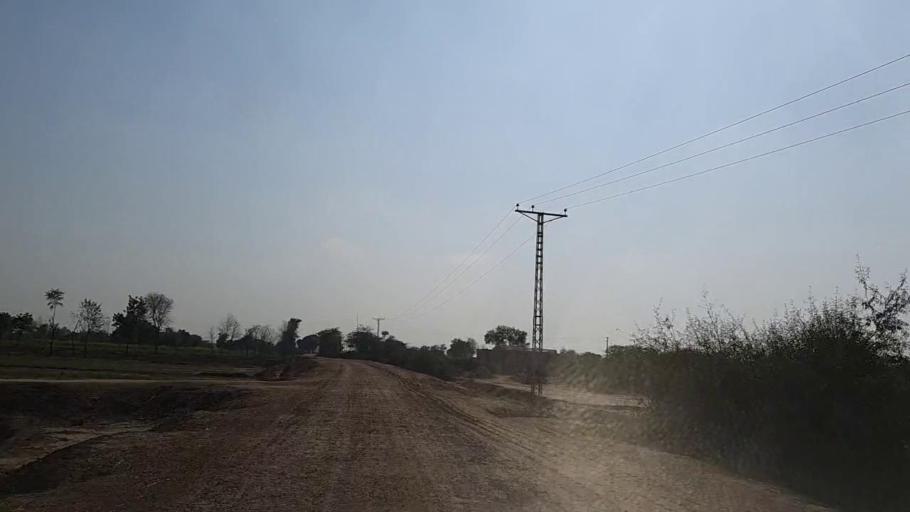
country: PK
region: Sindh
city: Daur
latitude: 26.4526
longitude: 68.2347
